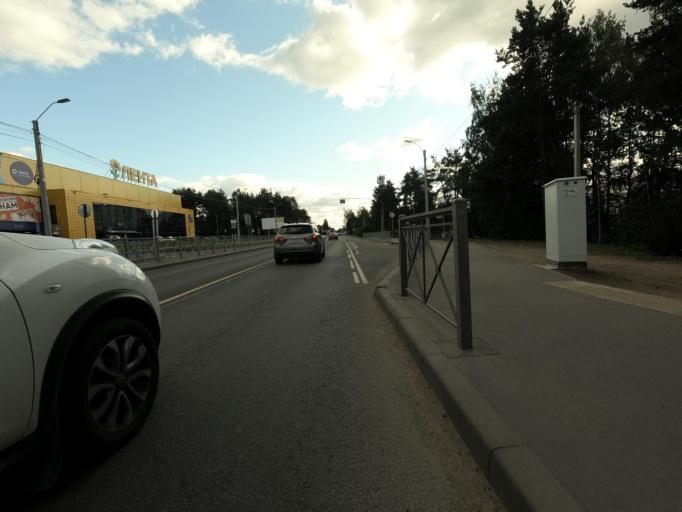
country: RU
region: Leningrad
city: Vsevolozhsk
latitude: 59.9914
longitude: 30.6581
